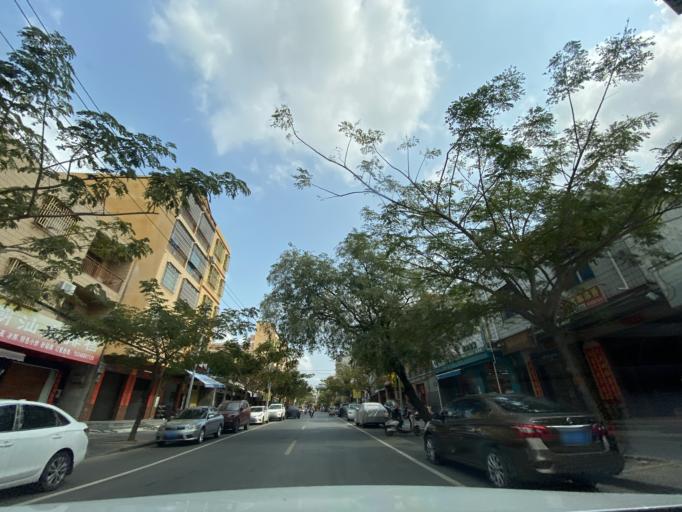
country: CN
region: Hainan
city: Yingzhou
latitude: 18.4207
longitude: 109.8501
